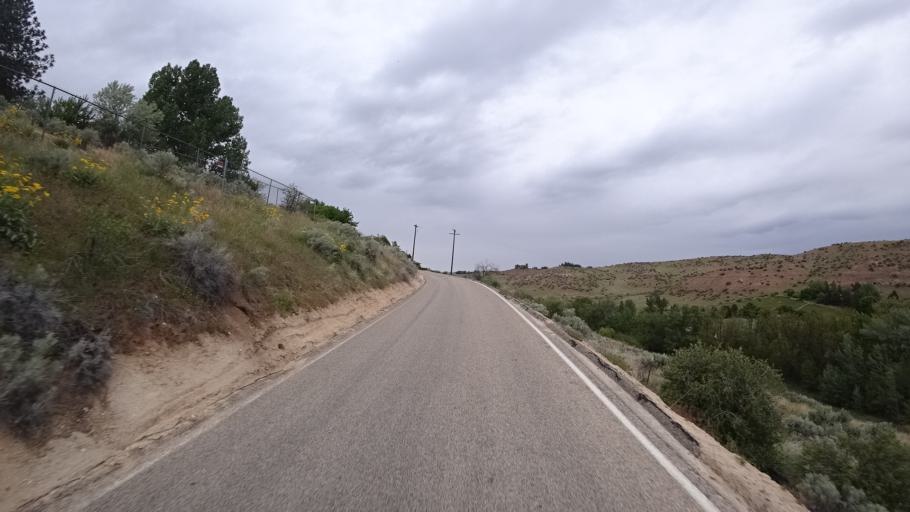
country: US
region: Idaho
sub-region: Ada County
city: Boise
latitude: 43.6167
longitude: -116.1655
